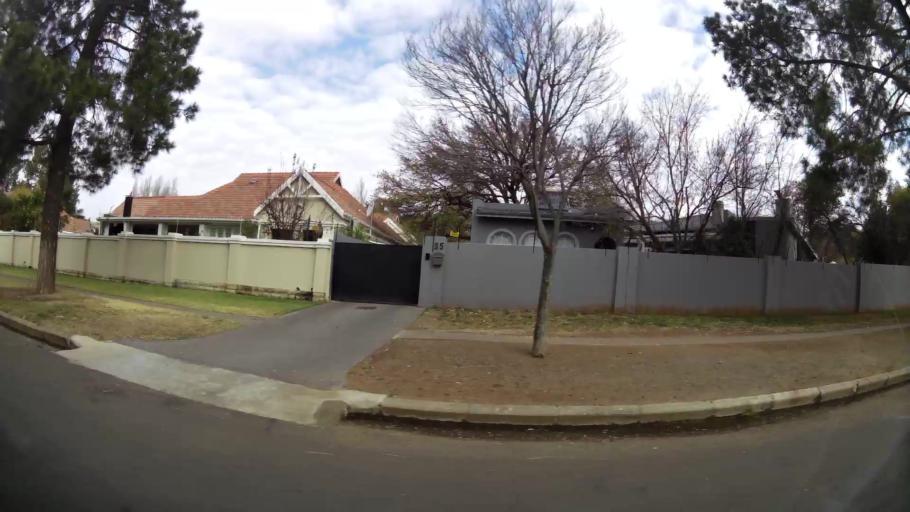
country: ZA
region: Orange Free State
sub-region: Mangaung Metropolitan Municipality
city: Bloemfontein
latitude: -29.0912
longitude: 26.2386
